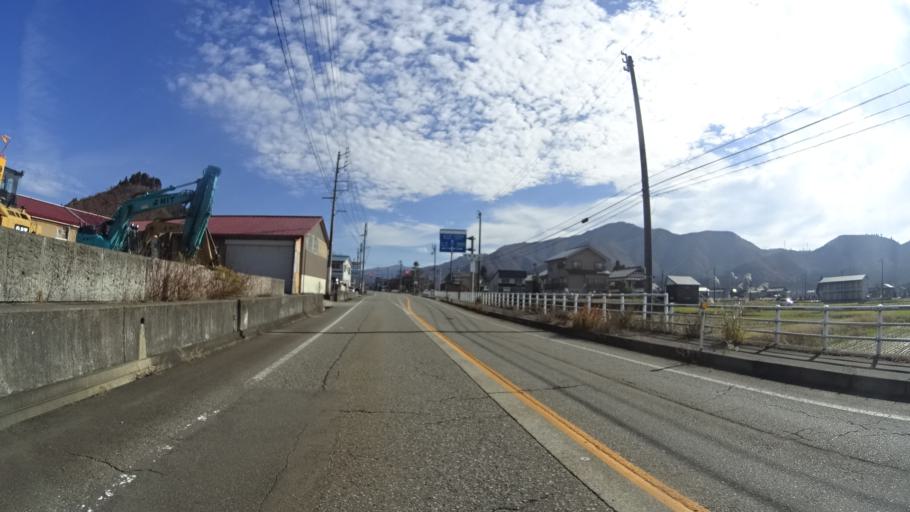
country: JP
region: Niigata
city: Muikamachi
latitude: 37.2291
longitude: 138.9830
